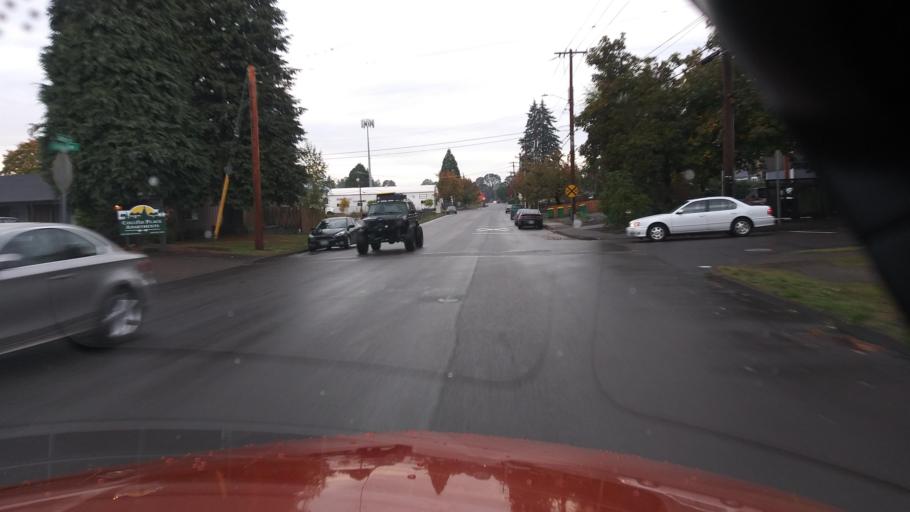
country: US
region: Oregon
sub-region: Washington County
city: Forest Grove
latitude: 45.5224
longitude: -123.0993
